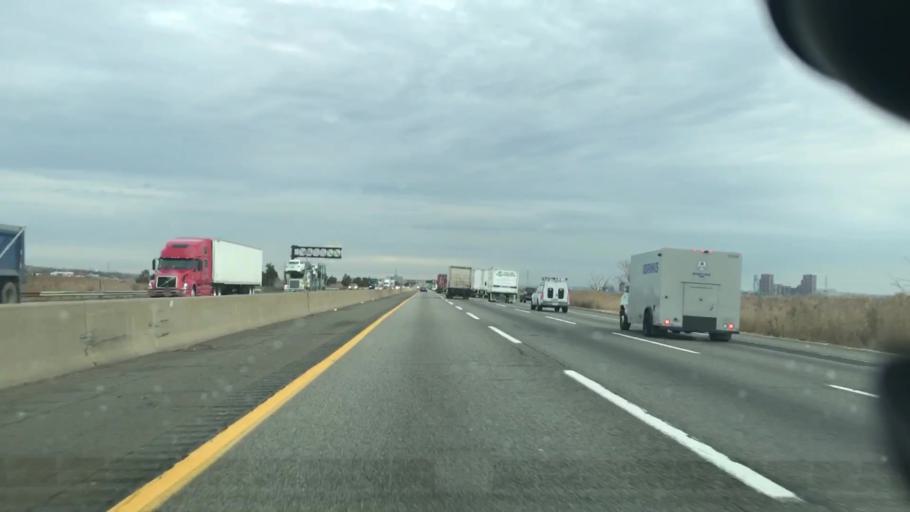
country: US
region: New Jersey
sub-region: Bergen County
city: North Arlington
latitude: 40.7672
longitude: -74.1091
